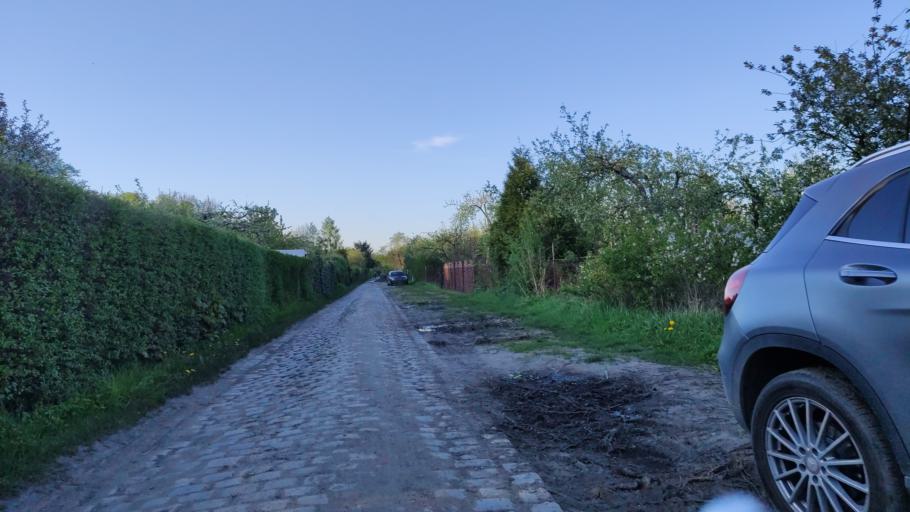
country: PL
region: Lower Silesian Voivodeship
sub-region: Powiat wroclawski
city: Wroclaw
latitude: 51.0768
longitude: 17.0275
